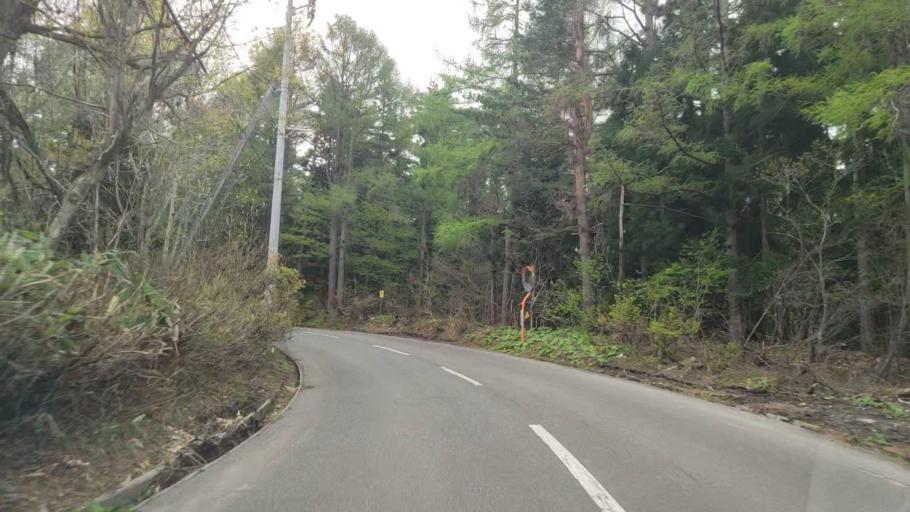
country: JP
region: Aomori
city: Aomori Shi
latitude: 40.7471
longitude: 140.8213
